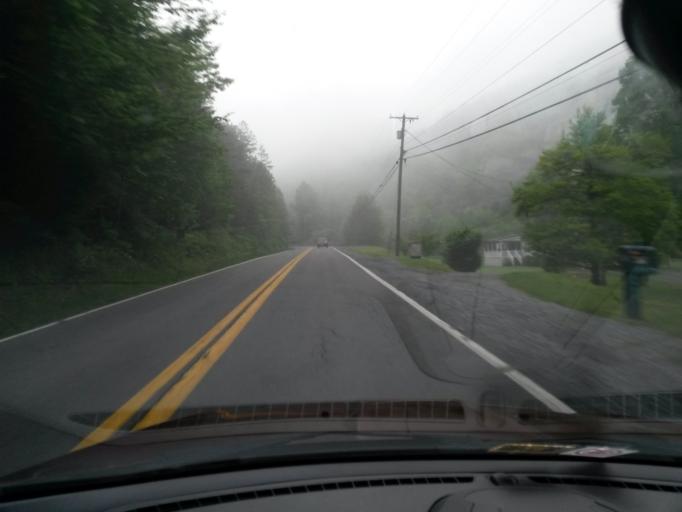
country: US
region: West Virginia
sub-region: McDowell County
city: Welch
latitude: 37.5017
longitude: -81.5486
